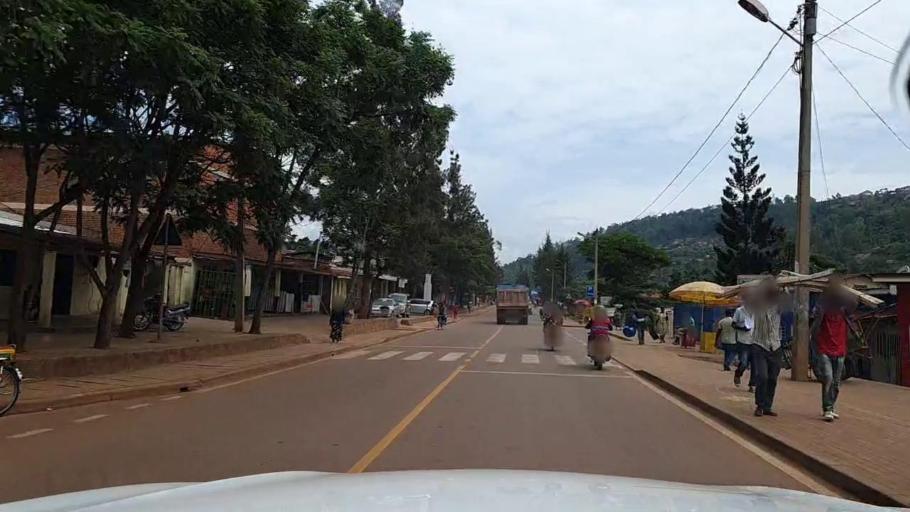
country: RW
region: Kigali
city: Kigali
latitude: -1.9226
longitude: 30.0469
